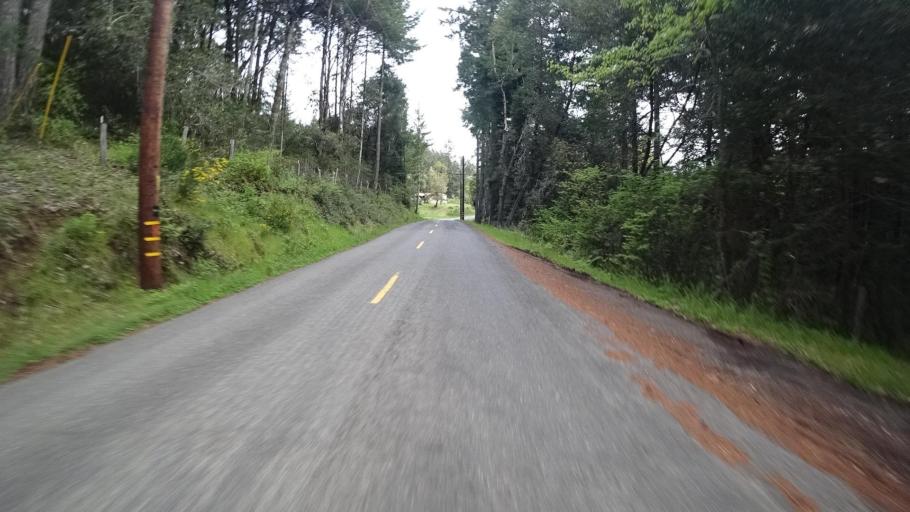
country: US
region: California
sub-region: Humboldt County
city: Redway
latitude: 40.2996
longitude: -123.8218
